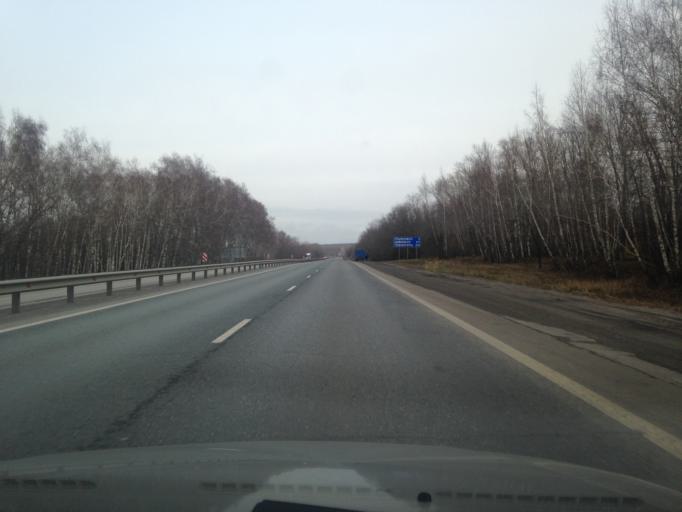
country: RU
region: Ulyanovsk
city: Novoul'yanovsk
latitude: 54.1980
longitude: 48.2859
